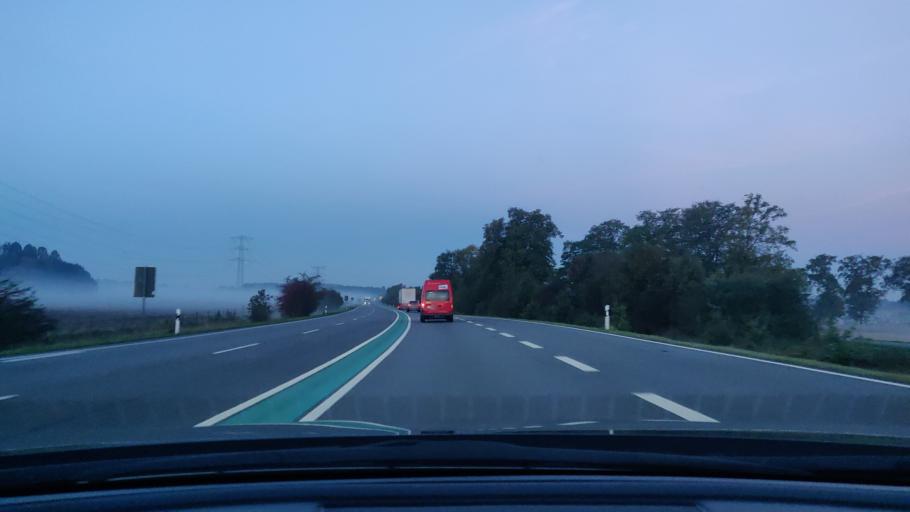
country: DE
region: North Rhine-Westphalia
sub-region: Regierungsbezirk Munster
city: Gronau
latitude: 52.1952
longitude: 6.9929
